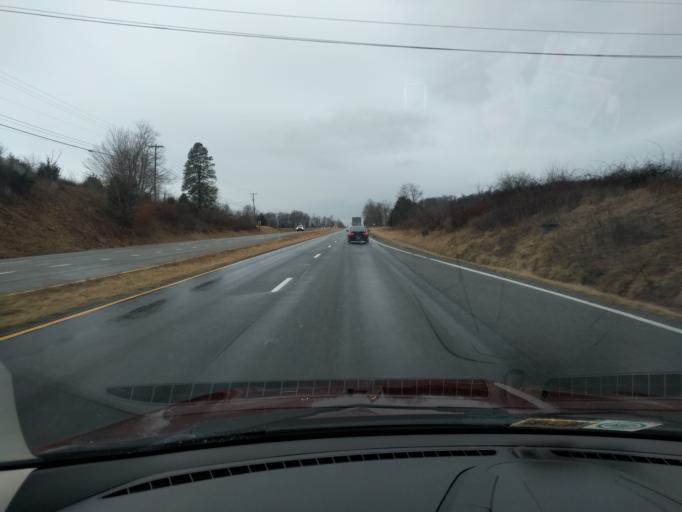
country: US
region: Virginia
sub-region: Giles County
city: Pembroke
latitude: 37.3128
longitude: -80.5823
